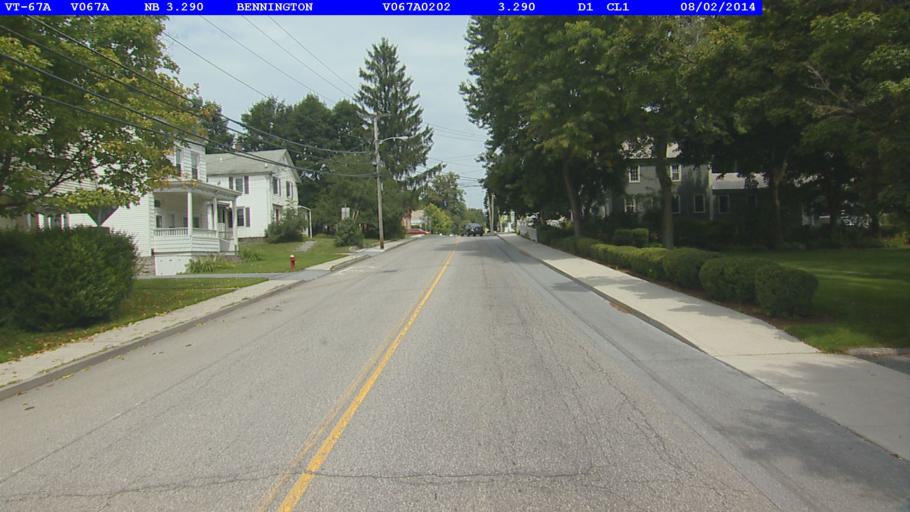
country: US
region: Vermont
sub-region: Bennington County
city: North Bennington
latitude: 42.9294
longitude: -73.2424
